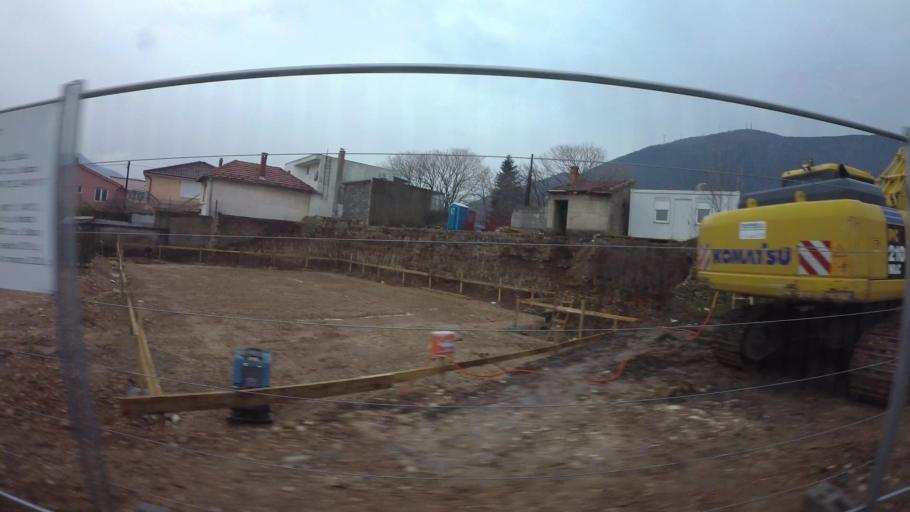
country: BA
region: Federation of Bosnia and Herzegovina
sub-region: Hercegovacko-Bosanski Kanton
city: Mostar
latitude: 43.3585
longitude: 17.8008
